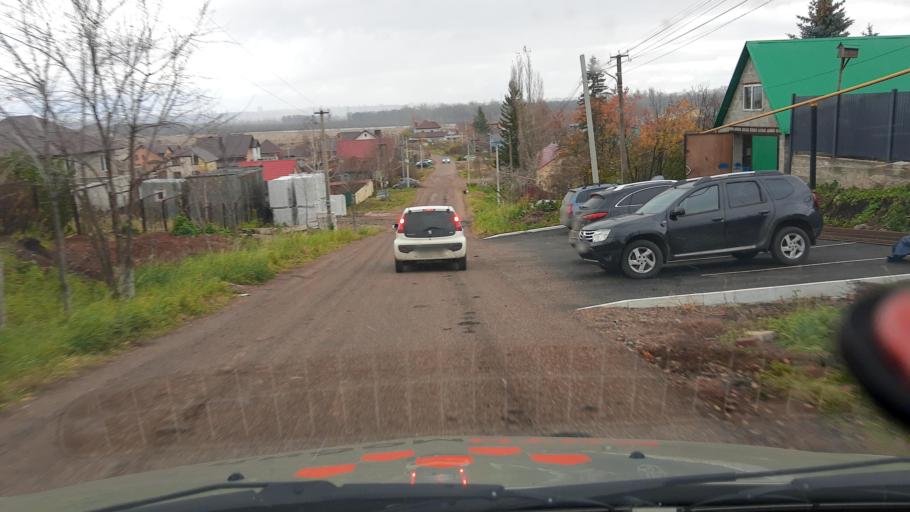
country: RU
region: Bashkortostan
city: Mikhaylovka
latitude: 54.8243
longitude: 55.9072
